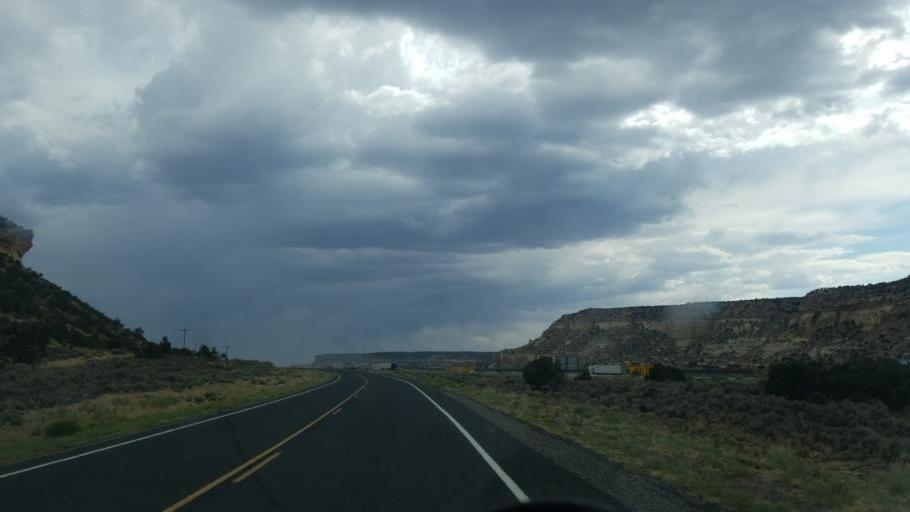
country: US
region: Arizona
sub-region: Apache County
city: Houck
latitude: 35.4107
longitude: -108.9962
